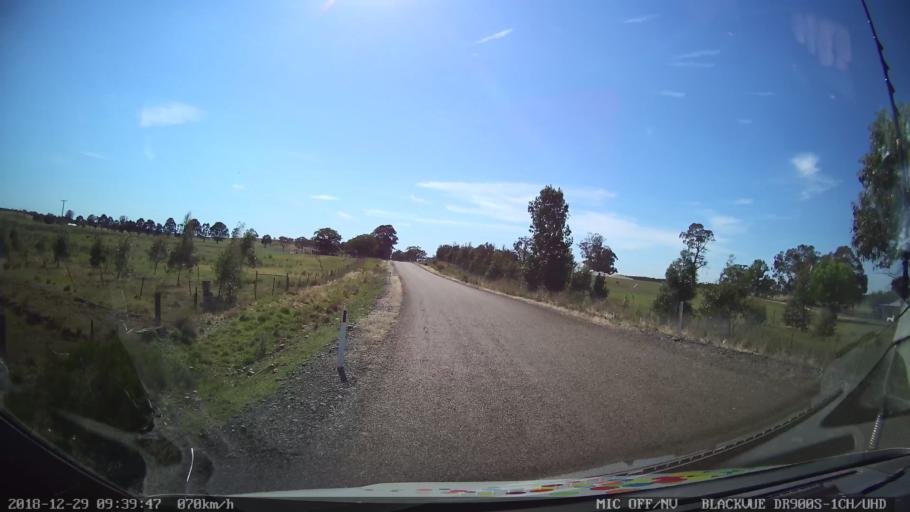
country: AU
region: New South Wales
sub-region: Upper Lachlan Shire
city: Crookwell
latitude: -34.6557
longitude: 149.3893
